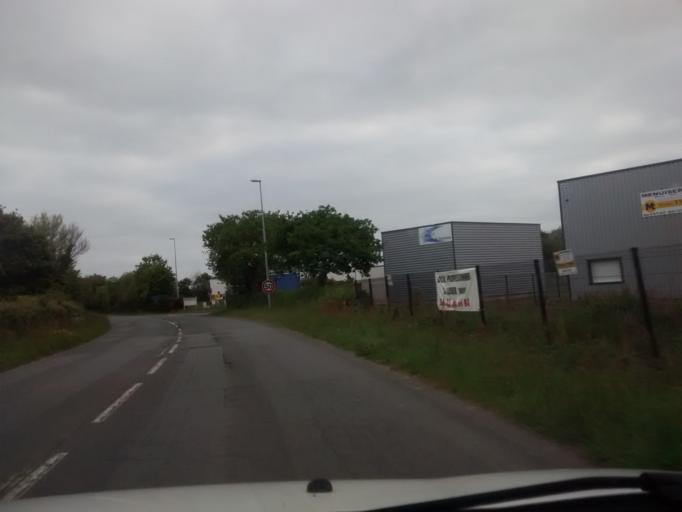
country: FR
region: Brittany
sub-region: Departement des Cotes-d'Armor
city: Tregastel
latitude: 48.8031
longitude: -3.4740
